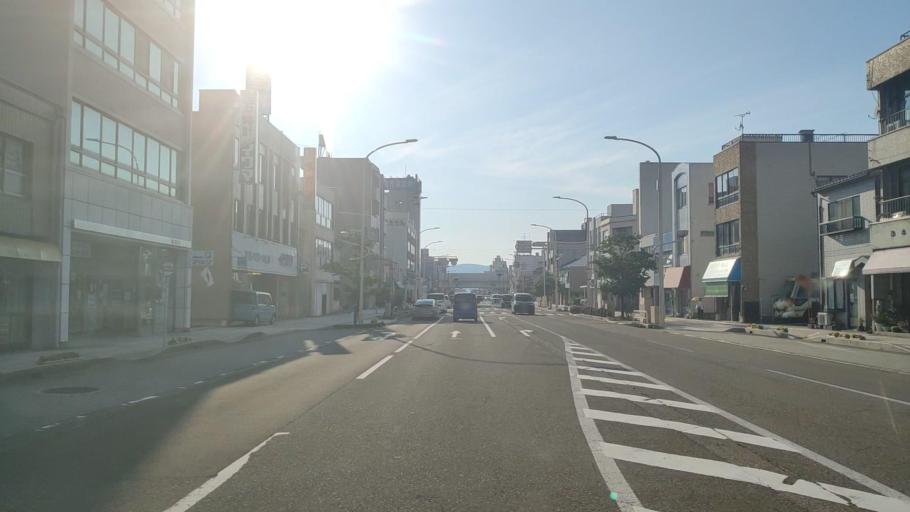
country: JP
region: Fukui
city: Fukui-shi
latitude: 36.0581
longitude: 136.2246
